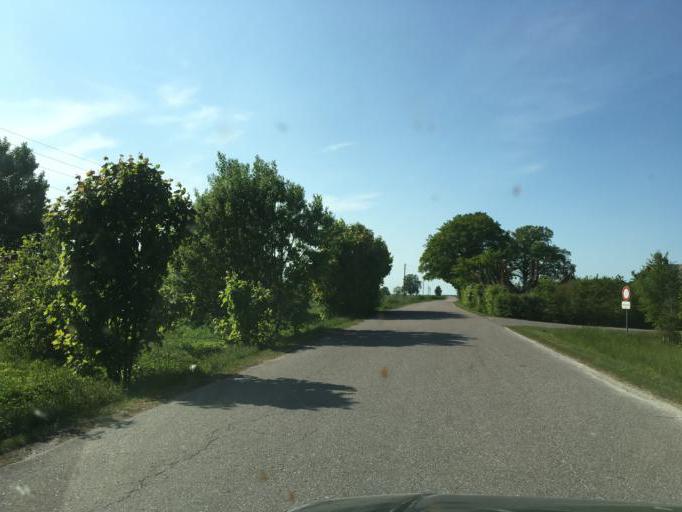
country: LV
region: Dundaga
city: Dundaga
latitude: 57.6077
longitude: 22.4475
